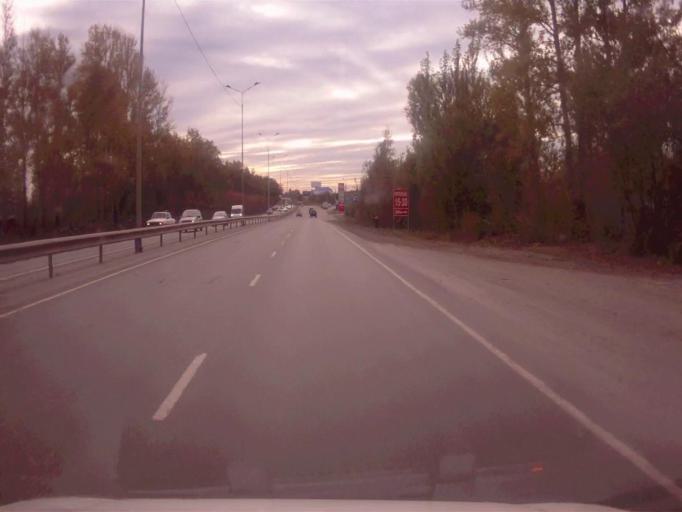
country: RU
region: Chelyabinsk
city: Novosineglazovskiy
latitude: 55.0845
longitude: 61.3955
